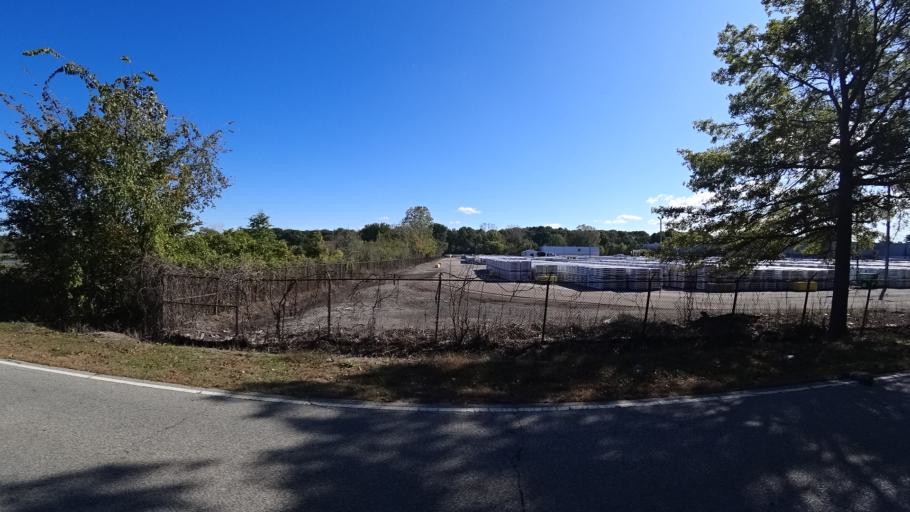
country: US
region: Indiana
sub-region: LaPorte County
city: Michigan City
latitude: 41.6845
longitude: -86.9133
